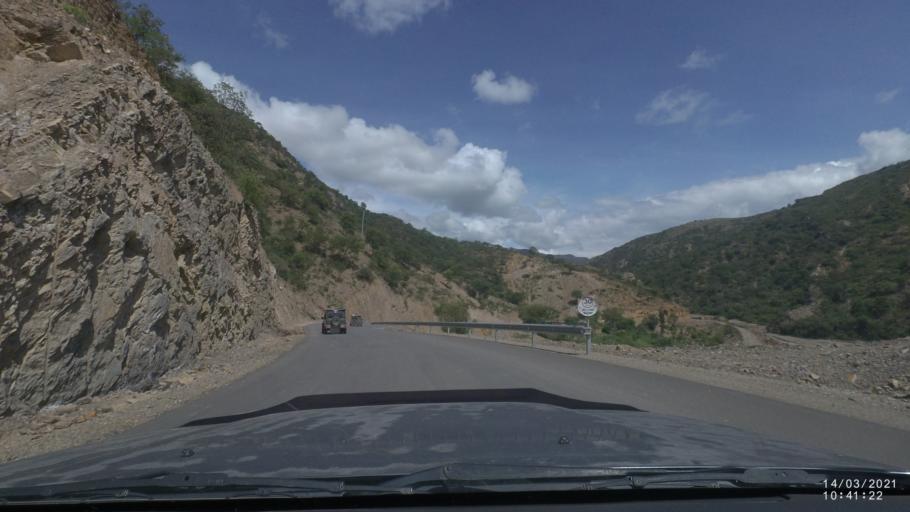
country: BO
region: Cochabamba
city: Tarata
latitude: -17.8799
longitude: -65.9110
